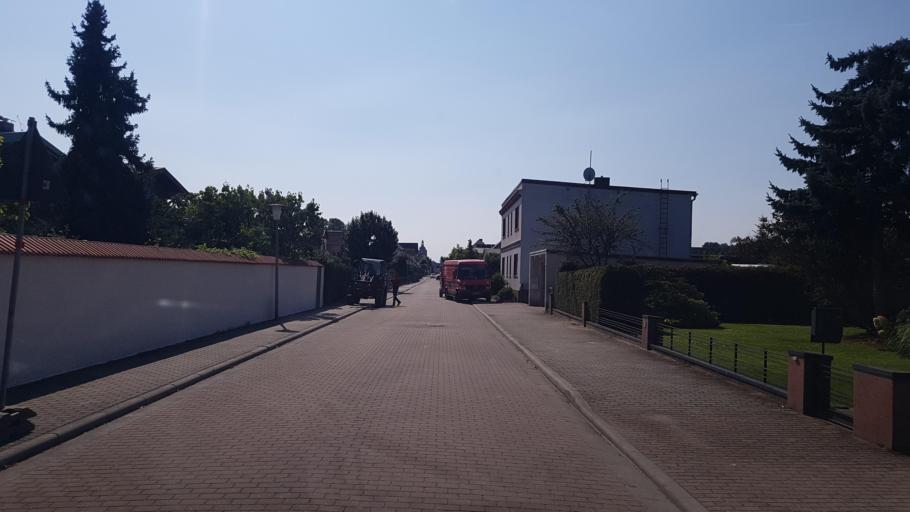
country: DE
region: Brandenburg
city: Vetschau
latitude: 51.7912
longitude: 14.0726
